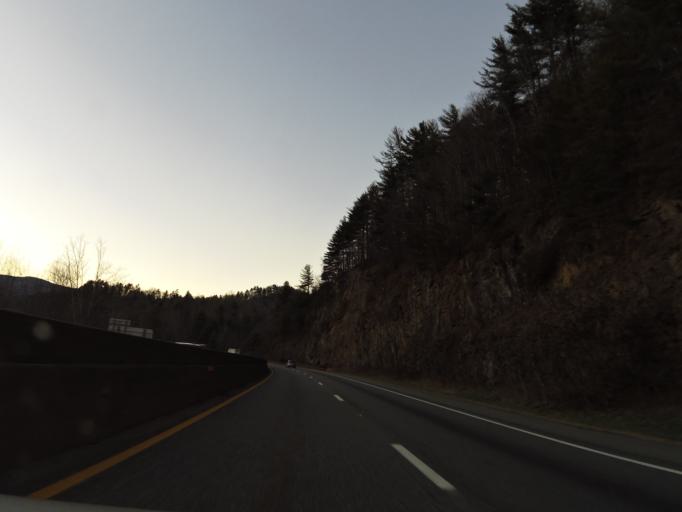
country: US
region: North Carolina
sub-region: Haywood County
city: Cove Creek
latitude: 35.6724
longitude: -83.0108
